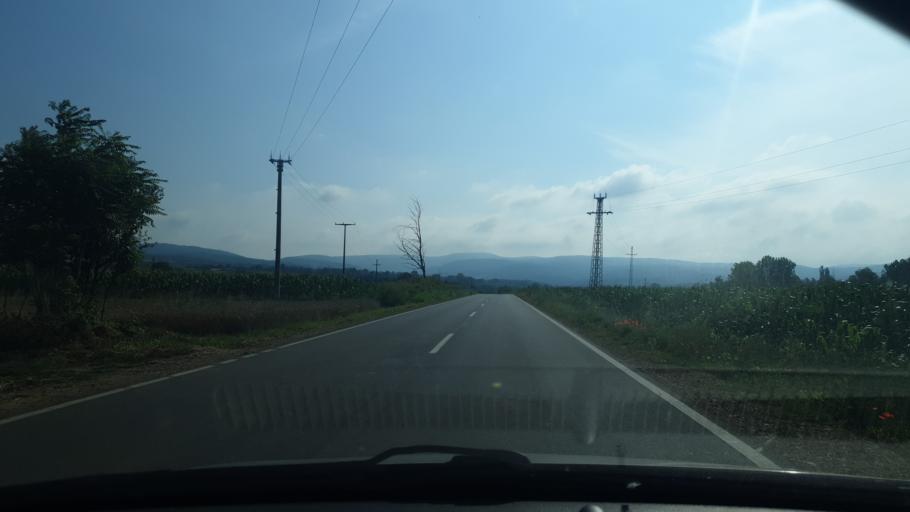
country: RS
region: Central Serbia
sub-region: Pomoravski Okrug
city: Cuprija
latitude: 43.9524
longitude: 21.4456
